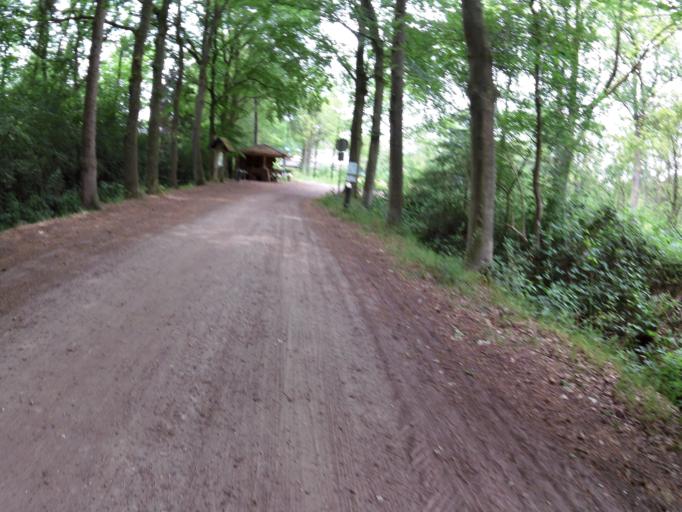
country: NL
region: North Brabant
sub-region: Gemeente Oirschot
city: Oirschot
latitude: 51.5384
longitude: 5.3380
